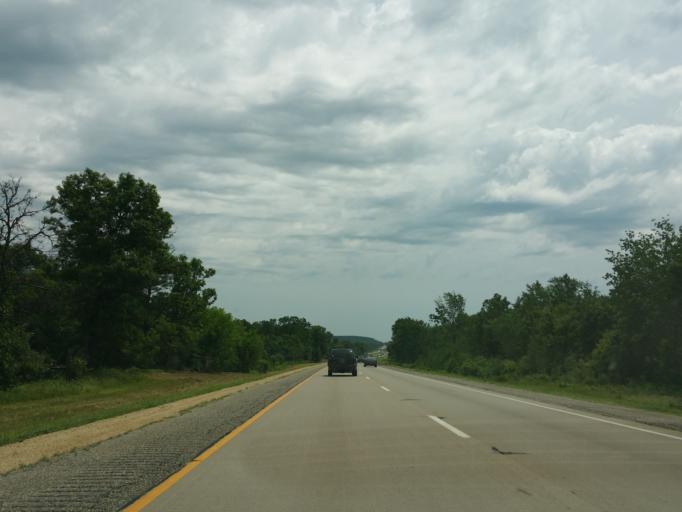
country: US
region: Wisconsin
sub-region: Columbia County
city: Wisconsin Dells
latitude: 43.6913
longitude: -89.8509
